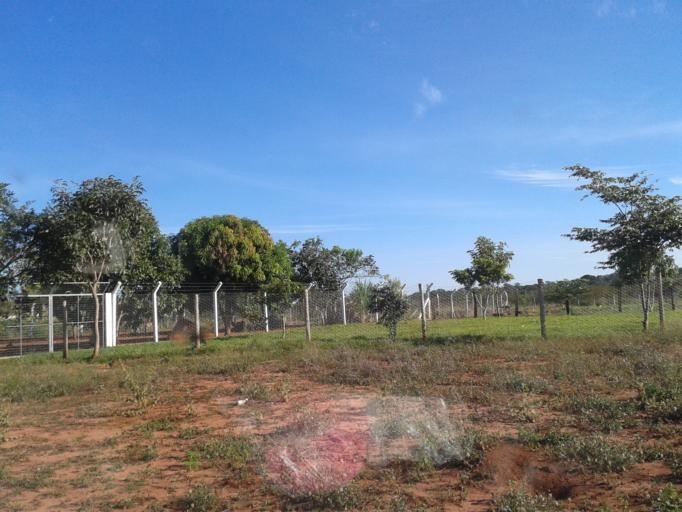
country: BR
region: Minas Gerais
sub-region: Santa Vitoria
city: Santa Vitoria
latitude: -19.0006
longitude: -50.3879
